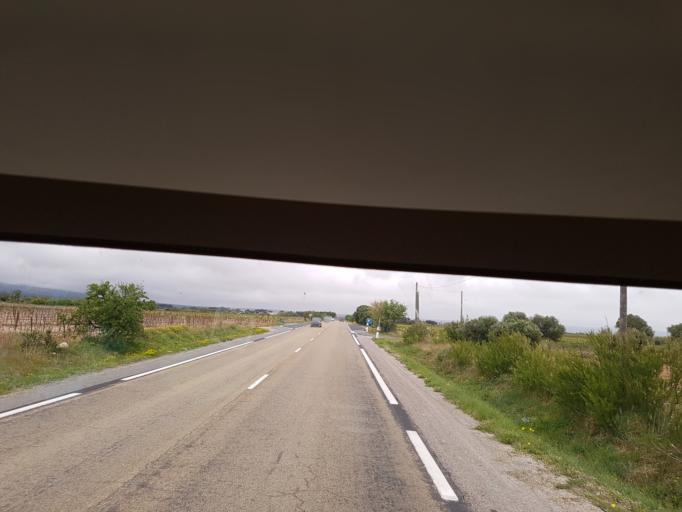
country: FR
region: Languedoc-Roussillon
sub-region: Departement de l'Aude
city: Leucate
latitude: 42.9238
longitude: 2.9950
